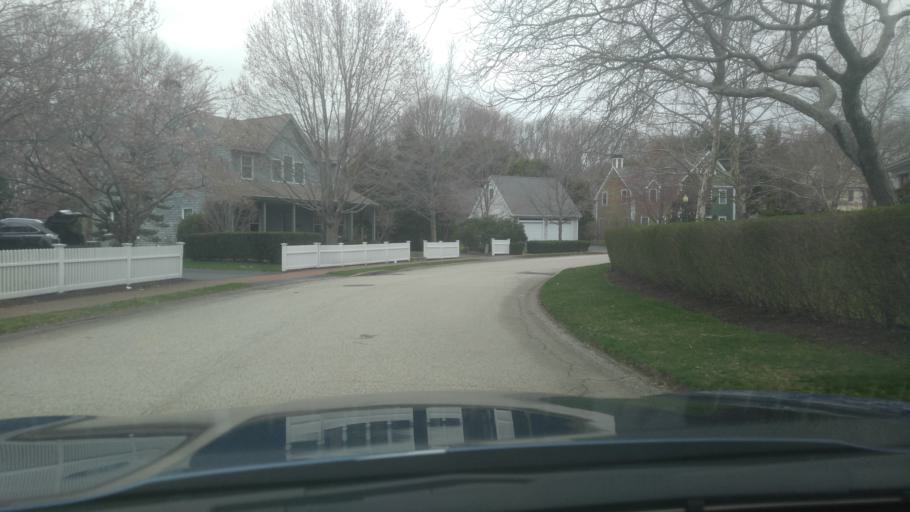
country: US
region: Rhode Island
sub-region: Washington County
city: North Kingstown
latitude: 41.5843
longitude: -71.4476
